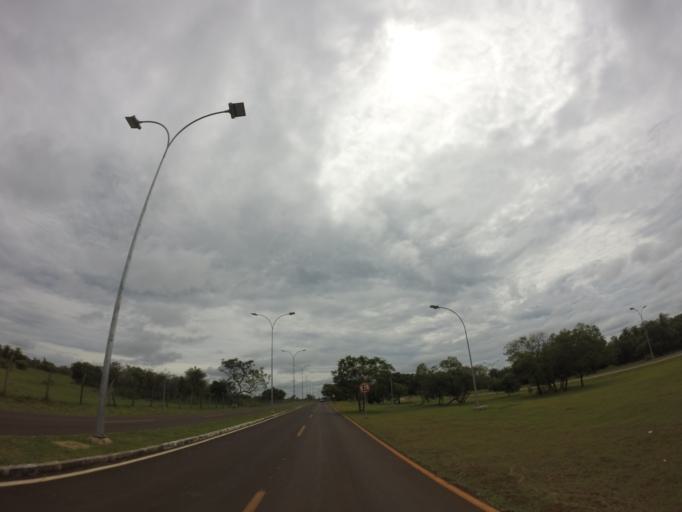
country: PY
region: Alto Parana
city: Ciudad del Este
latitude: -25.3908
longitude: -54.6336
